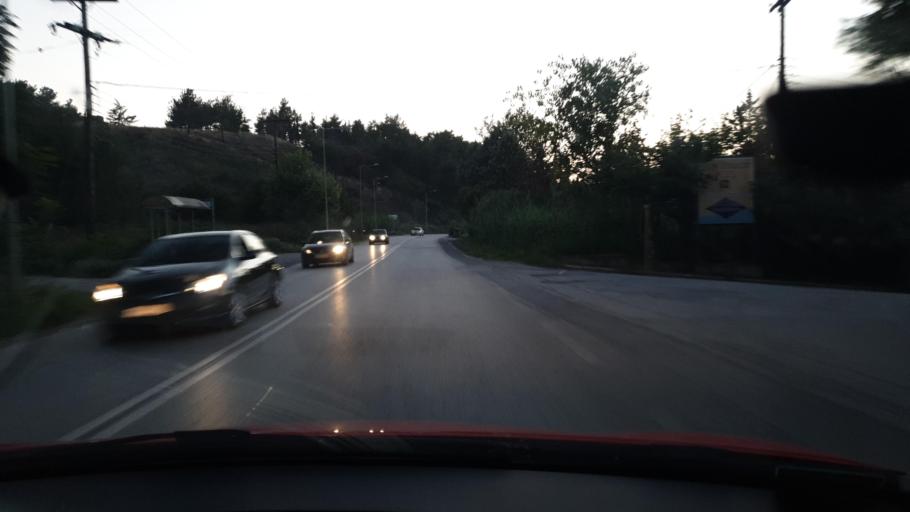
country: GR
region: Central Macedonia
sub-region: Nomos Thessalonikis
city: Agia Triada
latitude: 40.4986
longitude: 22.8820
